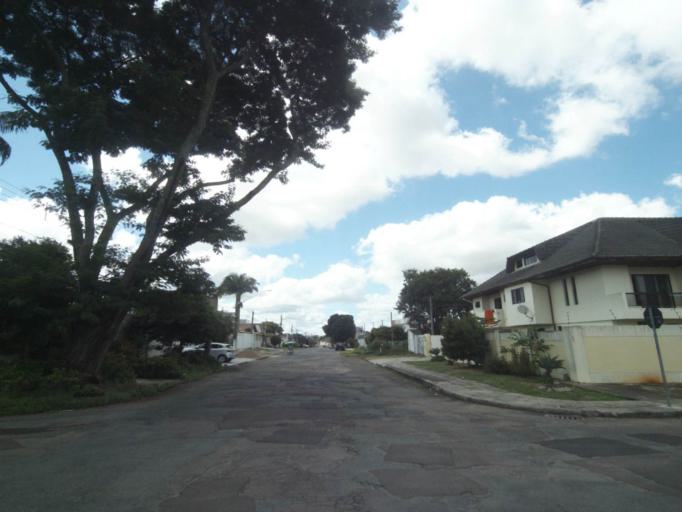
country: BR
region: Parana
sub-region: Pinhais
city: Pinhais
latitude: -25.4385
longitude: -49.2139
